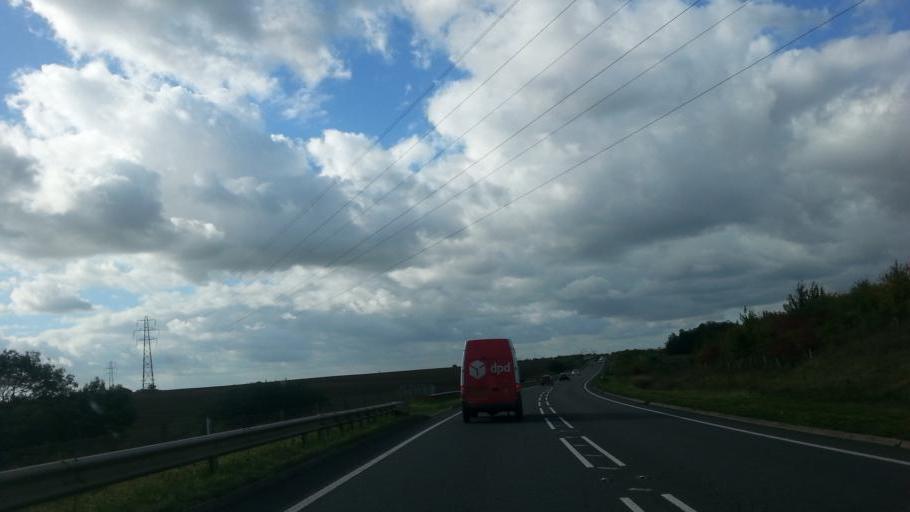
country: GB
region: England
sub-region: Cambridgeshire
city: Papworth Everard
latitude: 52.2409
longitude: -0.1173
